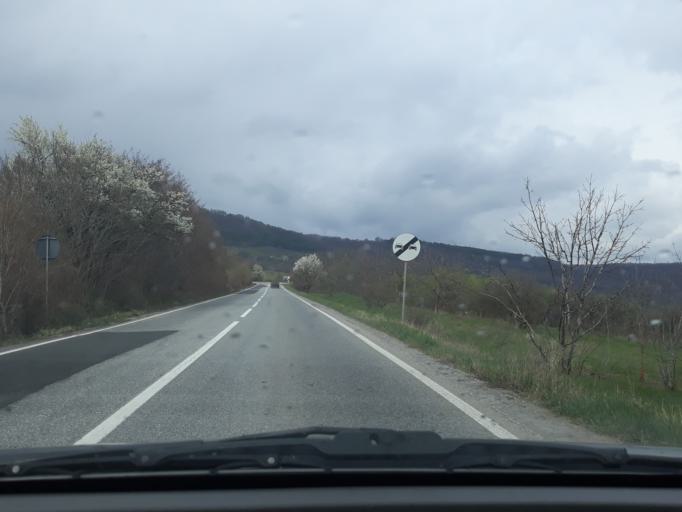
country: RO
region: Harghita
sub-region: Comuna Lupeni
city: Lupeni
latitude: 46.3980
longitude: 25.2156
